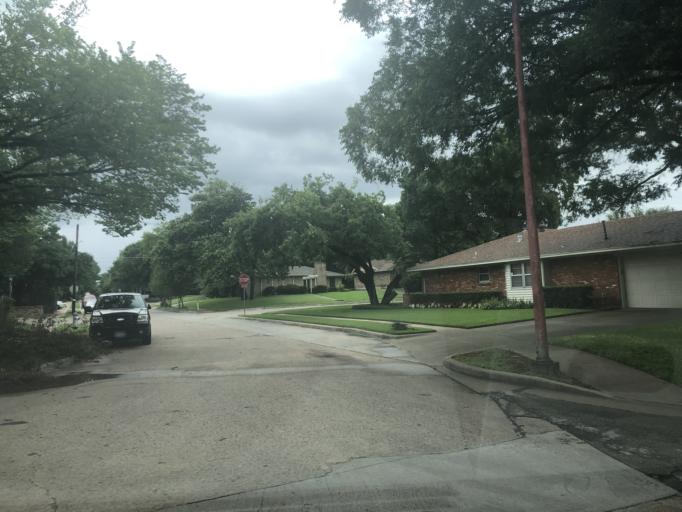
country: US
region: Texas
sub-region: Dallas County
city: Irving
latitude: 32.8032
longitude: -96.9442
